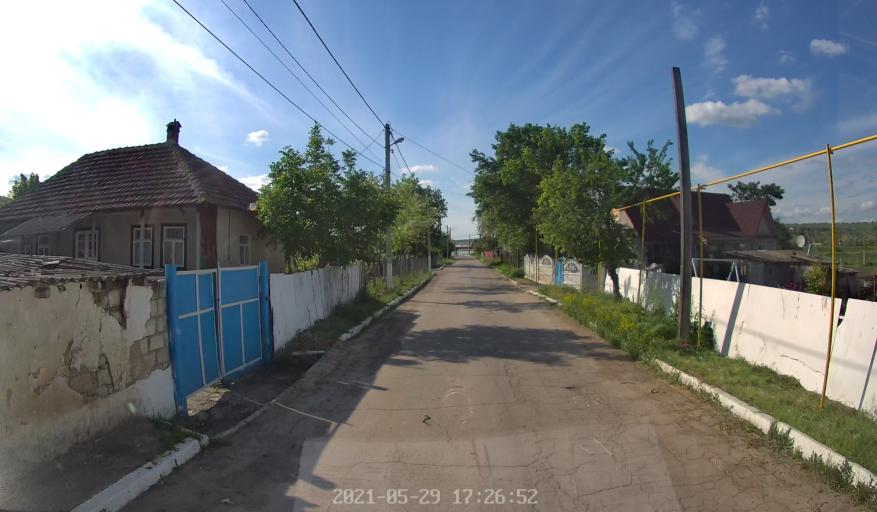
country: MD
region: Laloveni
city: Ialoveni
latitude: 46.8303
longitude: 28.8418
